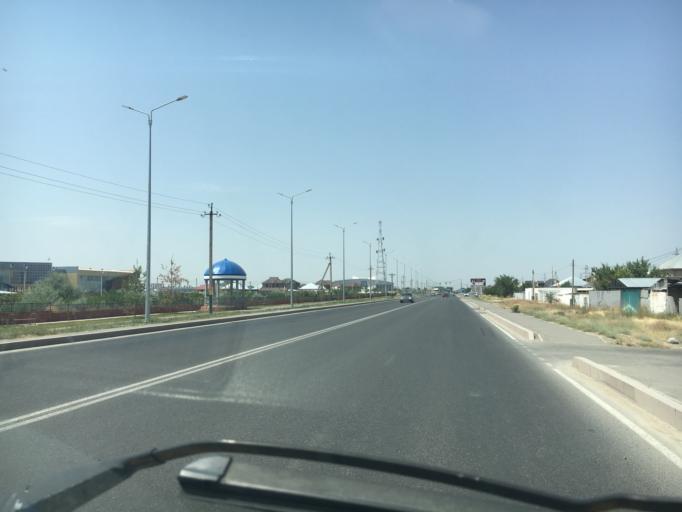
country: KZ
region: Zhambyl
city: Taraz
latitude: 42.8808
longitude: 71.3227
